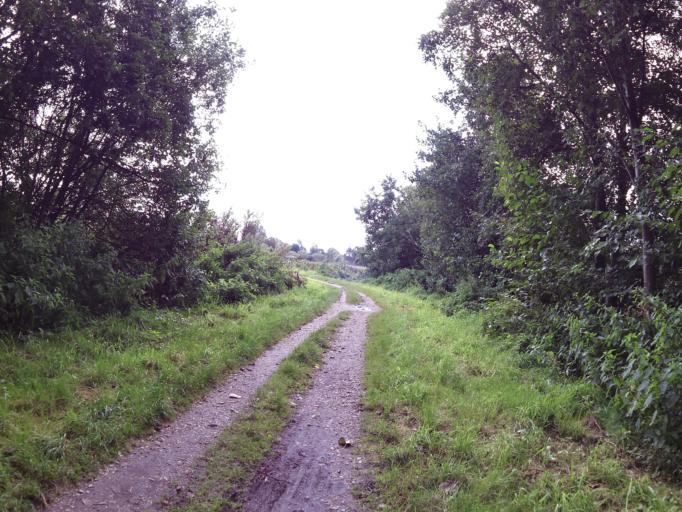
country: DE
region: Schleswig-Holstein
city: Wisch
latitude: 54.4245
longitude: 10.3659
